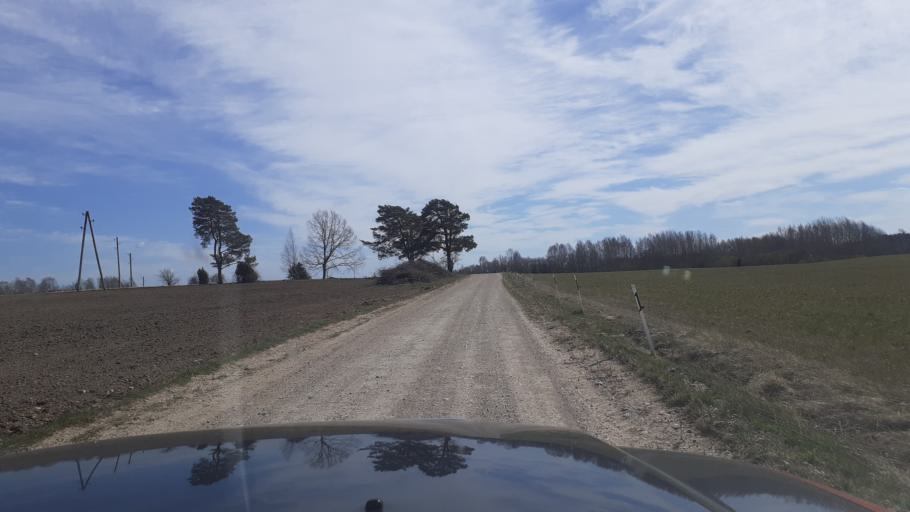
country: LV
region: Kuldigas Rajons
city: Kuldiga
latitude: 56.8391
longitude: 21.9907
